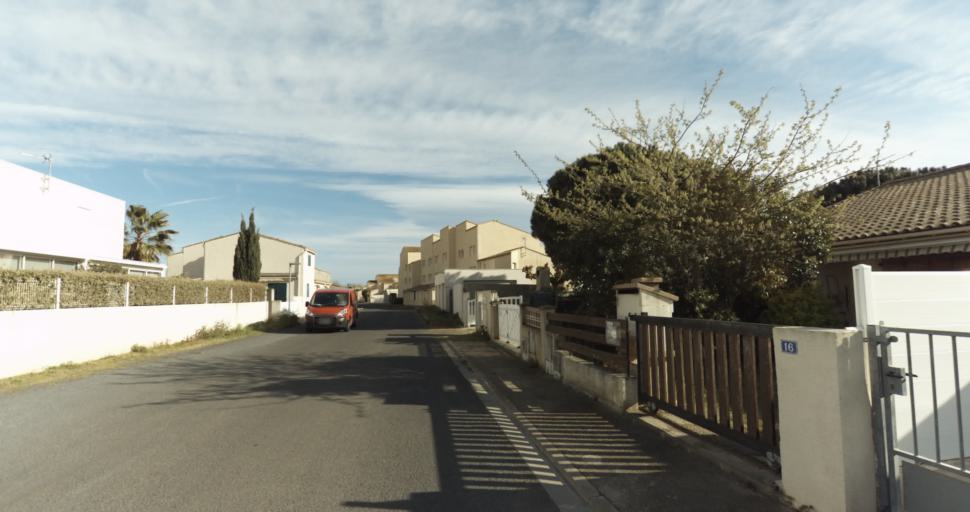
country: FR
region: Languedoc-Roussillon
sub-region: Departement de l'Herault
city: Marseillan
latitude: 43.3160
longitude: 3.5457
